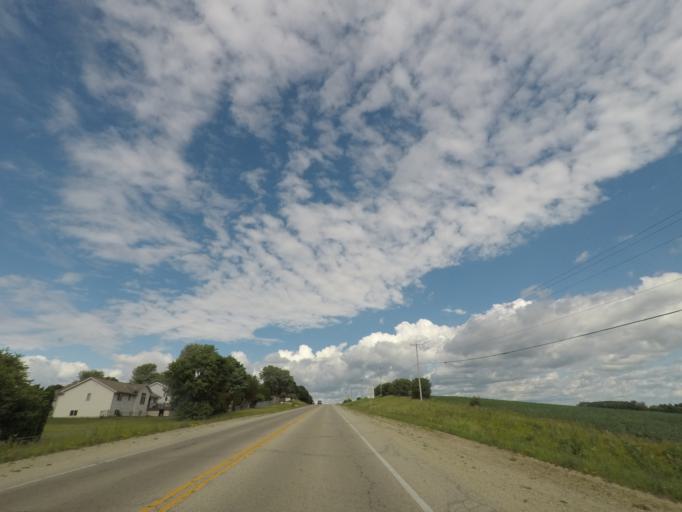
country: US
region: Wisconsin
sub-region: Rock County
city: Janesville
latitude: 42.6791
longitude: -89.0657
